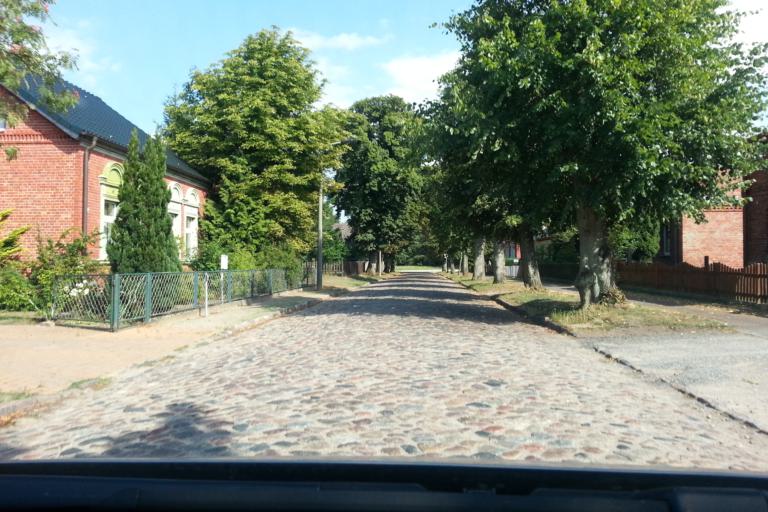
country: DE
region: Mecklenburg-Vorpommern
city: Ferdinandshof
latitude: 53.6293
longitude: 13.8638
